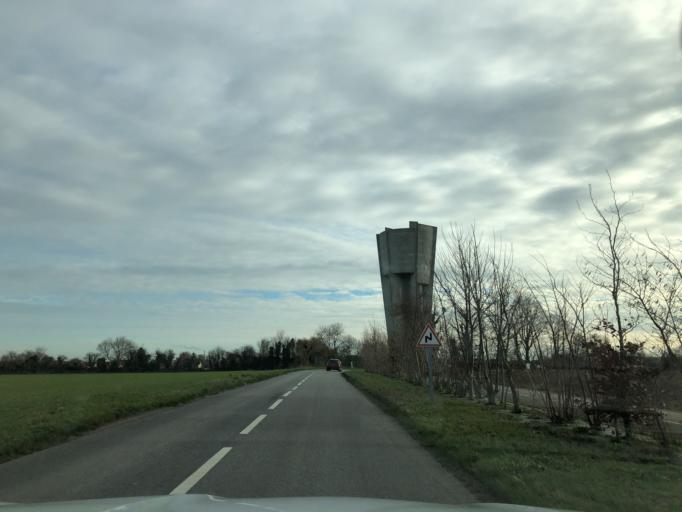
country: FR
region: Lower Normandy
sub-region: Departement du Calvados
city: Blainville-sur-Orne
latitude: 49.2355
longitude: -0.3106
